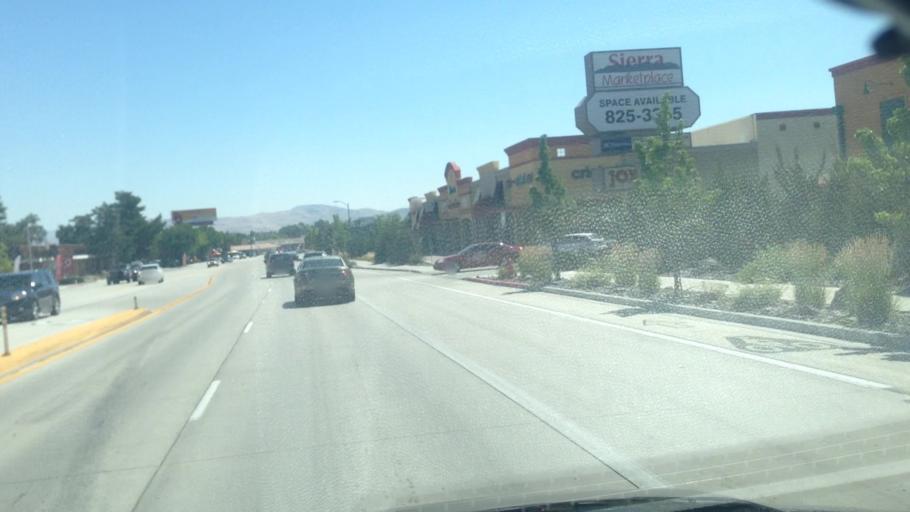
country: US
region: Nevada
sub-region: Washoe County
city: Reno
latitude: 39.4920
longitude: -119.7962
